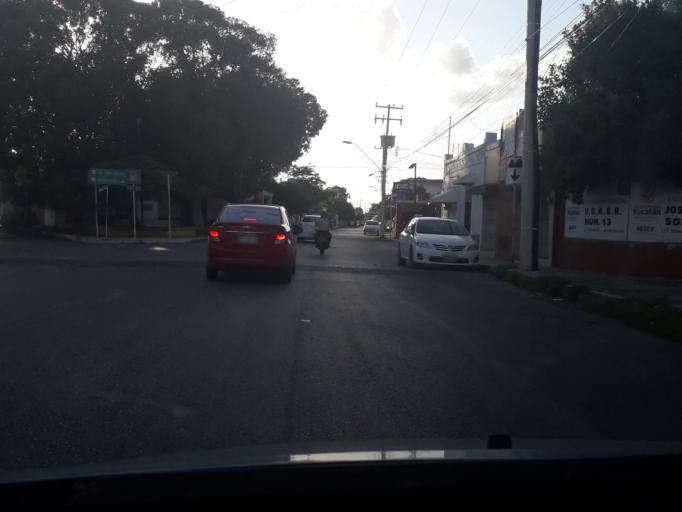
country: MX
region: Yucatan
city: Merida
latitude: 20.9664
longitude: -89.6447
